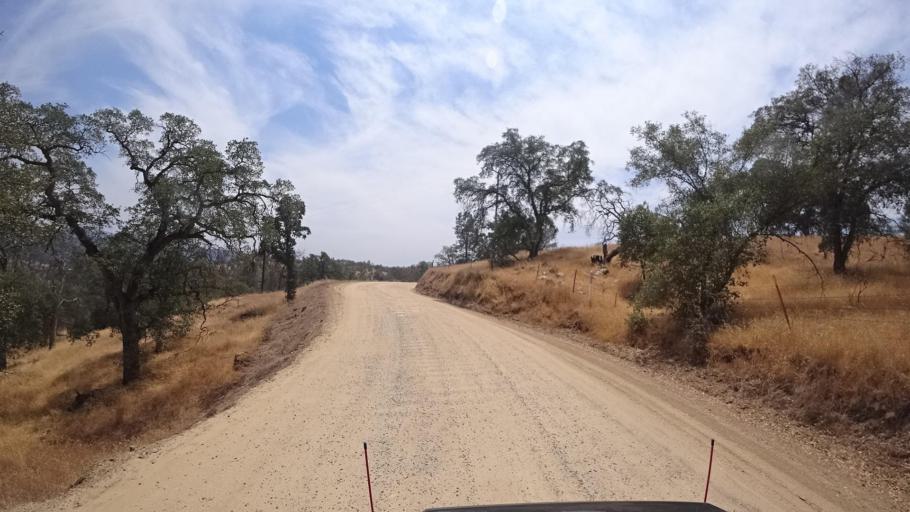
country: US
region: California
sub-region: Mariposa County
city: Mariposa
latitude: 37.3753
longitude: -119.8725
